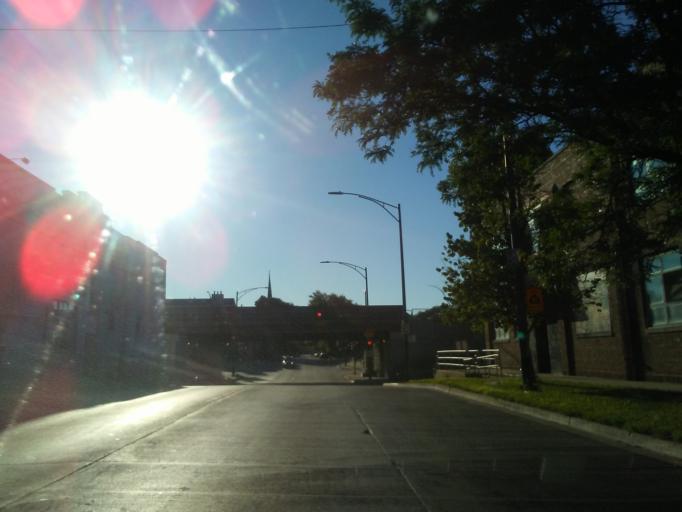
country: US
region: Illinois
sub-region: Cook County
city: Lincolnwood
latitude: 41.9761
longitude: -87.6755
